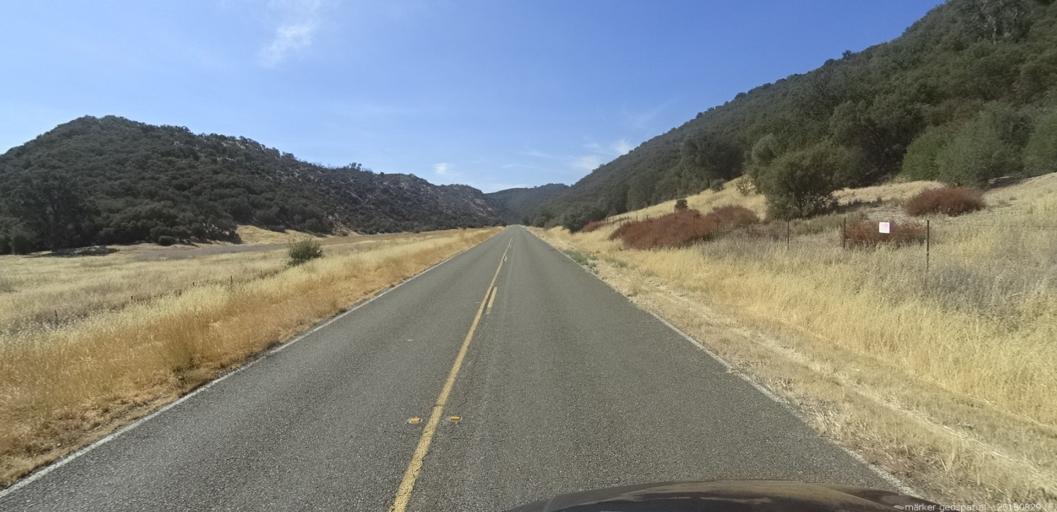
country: US
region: California
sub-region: San Luis Obispo County
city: Lake Nacimiento
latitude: 35.8701
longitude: -121.0629
